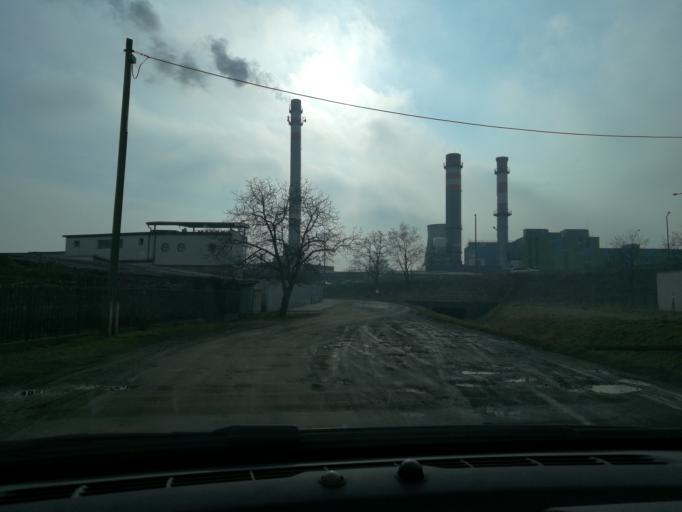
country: HU
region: Szabolcs-Szatmar-Bereg
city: Nyiregyhaza
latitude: 47.9585
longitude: 21.6991
